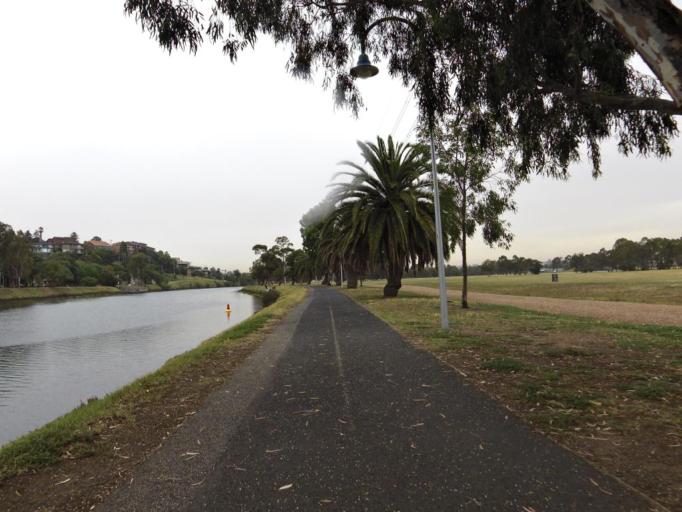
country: AU
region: Victoria
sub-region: Maribyrnong
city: Maribyrnong
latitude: -37.7770
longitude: 144.8972
